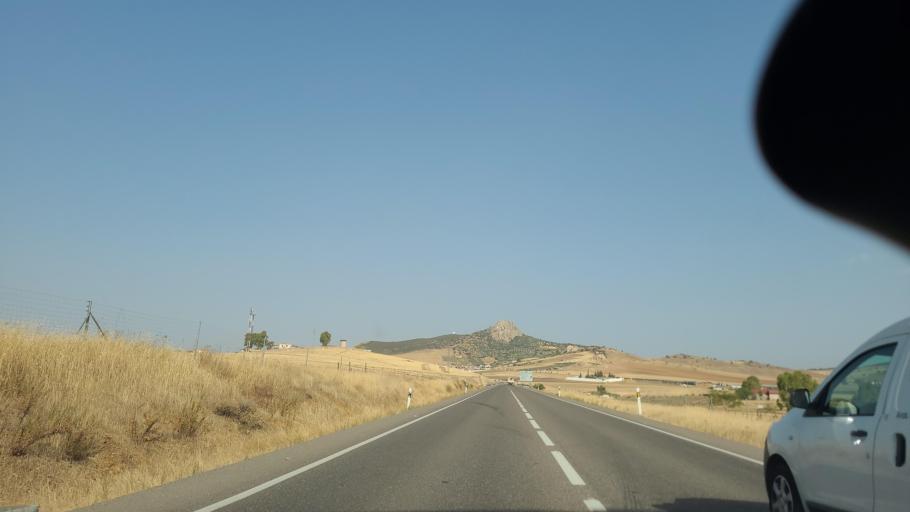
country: ES
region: Andalusia
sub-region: Province of Cordoba
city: Penarroya-Pueblonuevo
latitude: 38.3067
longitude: -5.2604
